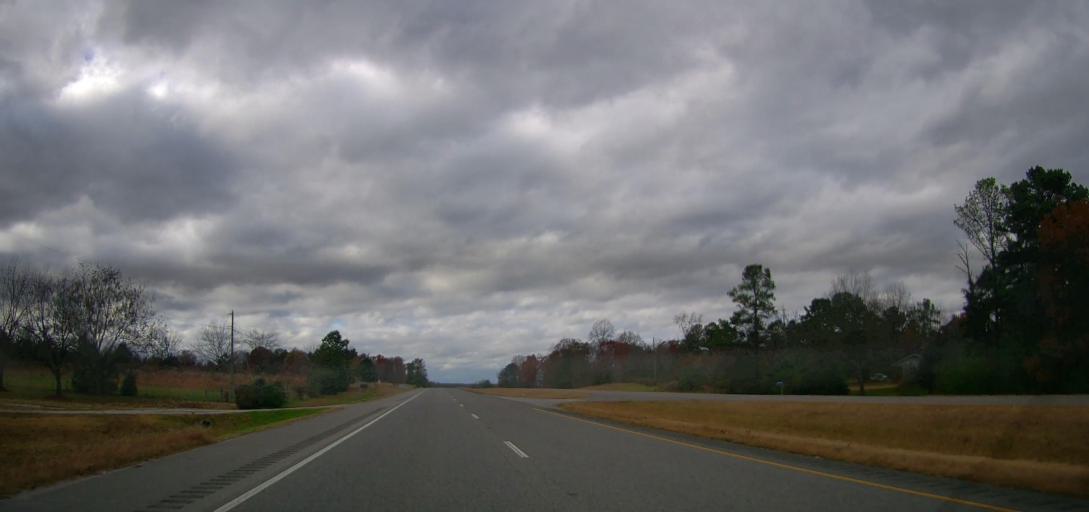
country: US
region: Alabama
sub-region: Lawrence County
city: Town Creek
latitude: 34.5971
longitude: -87.4381
